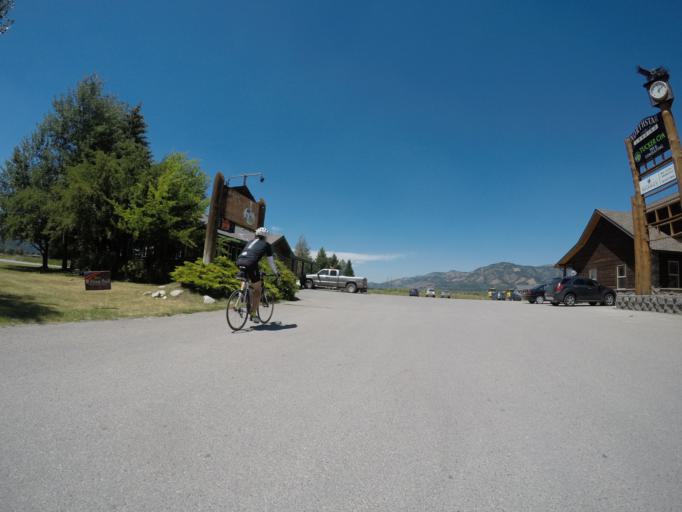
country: US
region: Wyoming
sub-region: Teton County
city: Hoback
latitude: 43.1617
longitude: -111.0229
